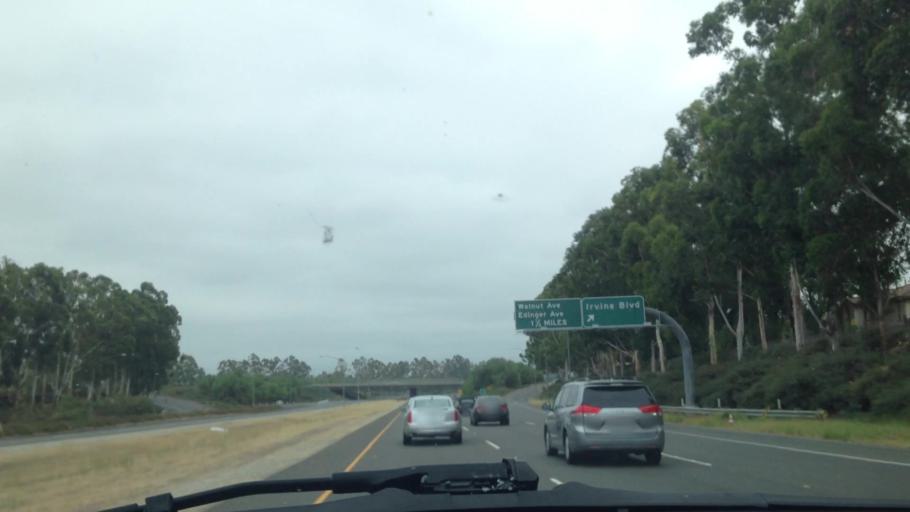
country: US
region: California
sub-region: Orange County
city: North Tustin
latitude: 33.7300
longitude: -117.7757
